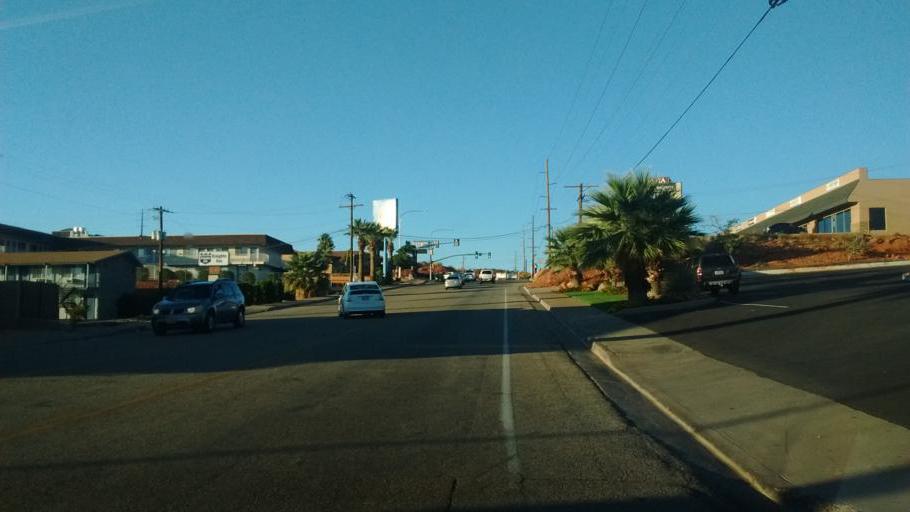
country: US
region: Utah
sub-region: Washington County
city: Saint George
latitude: 37.1107
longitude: -113.5621
